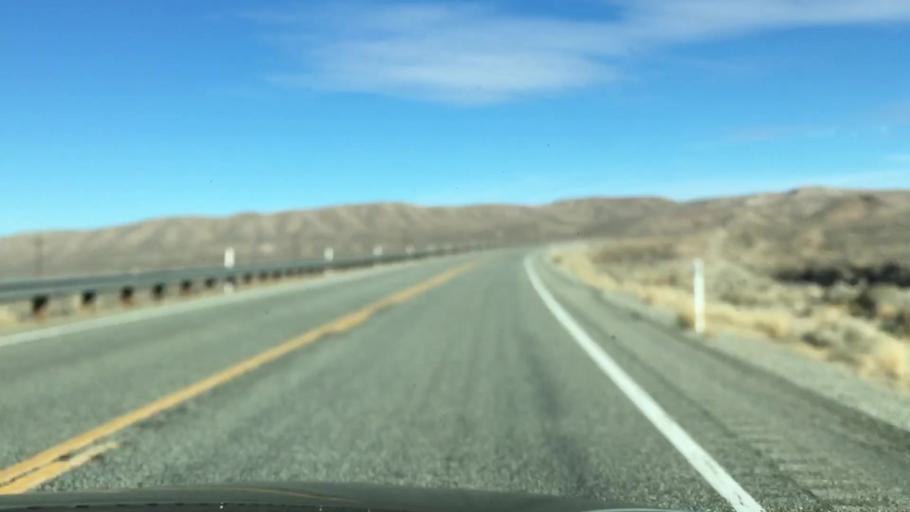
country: US
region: Nevada
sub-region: Lyon County
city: Yerington
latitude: 39.0446
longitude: -118.9791
